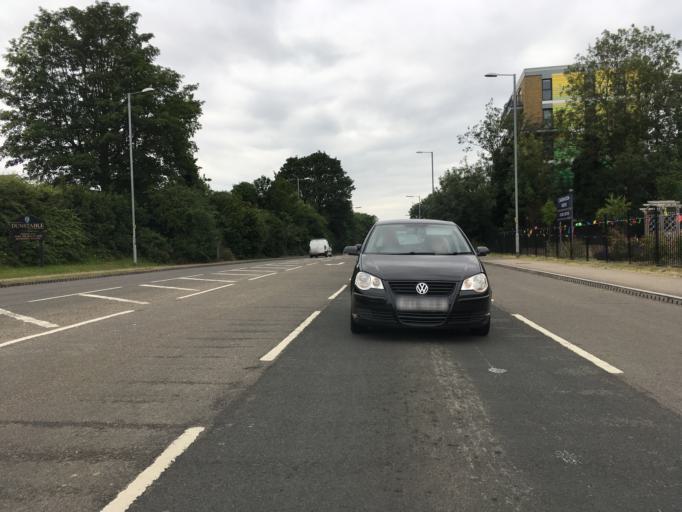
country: GB
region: England
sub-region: Central Bedfordshire
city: Kensworth
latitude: 51.8737
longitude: -0.5020
